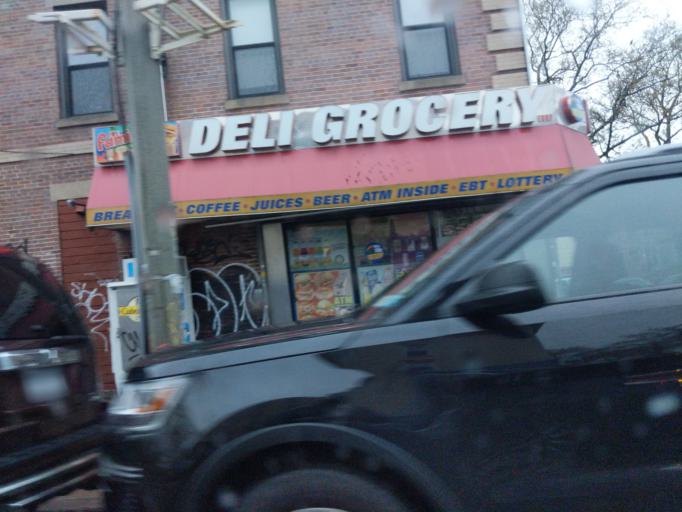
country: US
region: New York
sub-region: Kings County
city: East New York
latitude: 40.6955
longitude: -73.9082
